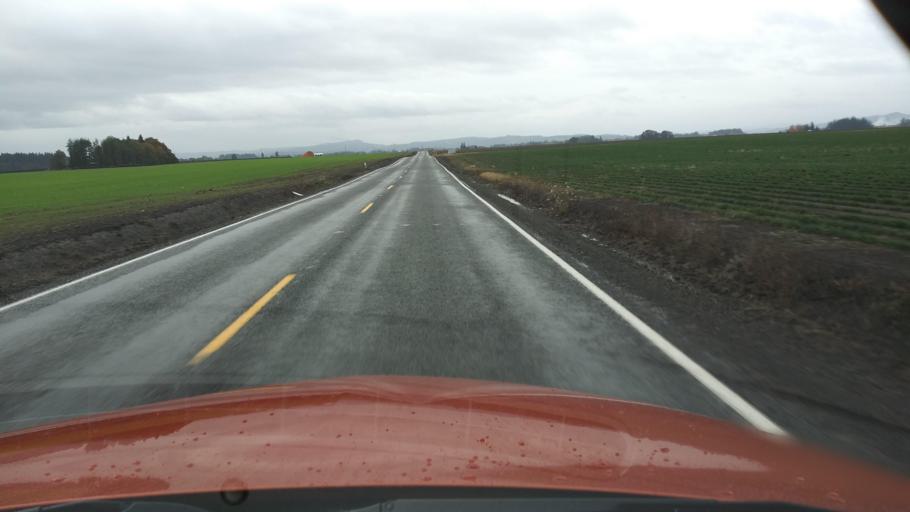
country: US
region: Oregon
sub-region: Washington County
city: North Plains
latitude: 45.5804
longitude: -123.0193
